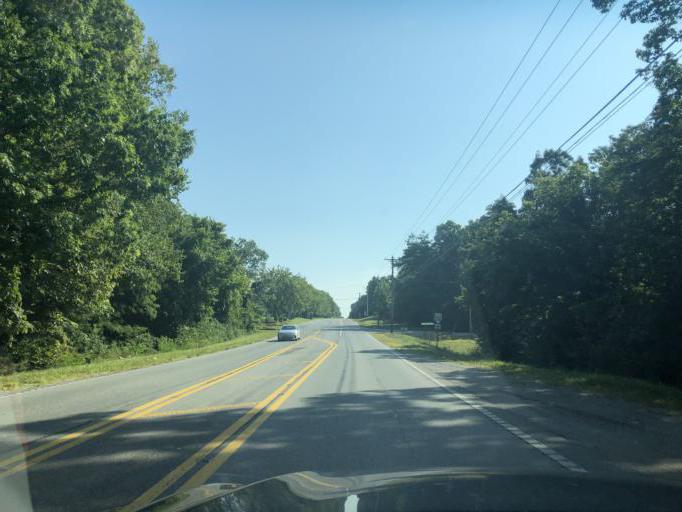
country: US
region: Tennessee
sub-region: Franklin County
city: Sewanee
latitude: 35.2128
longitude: -85.8933
